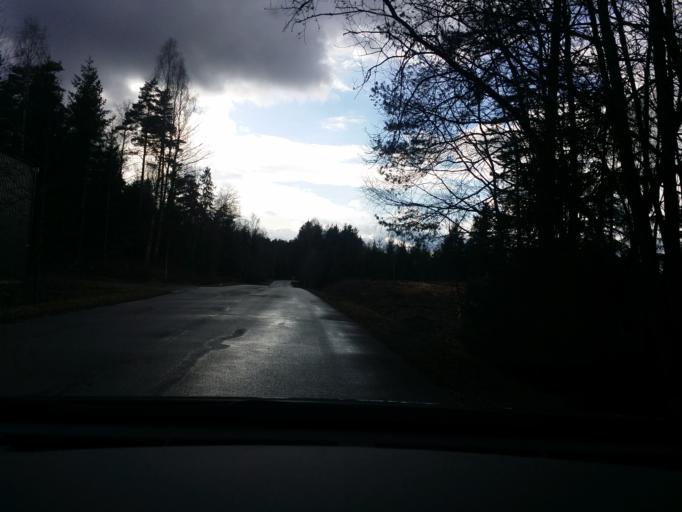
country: SE
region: Soedermanland
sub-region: Eskilstuna Kommun
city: Arla
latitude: 59.2947
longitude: 16.6983
